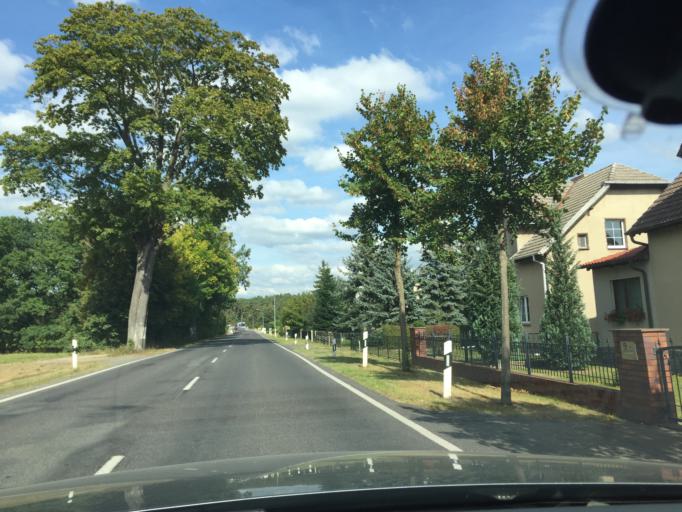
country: DE
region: Brandenburg
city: Spreenhagen
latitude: 52.3622
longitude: 13.8398
